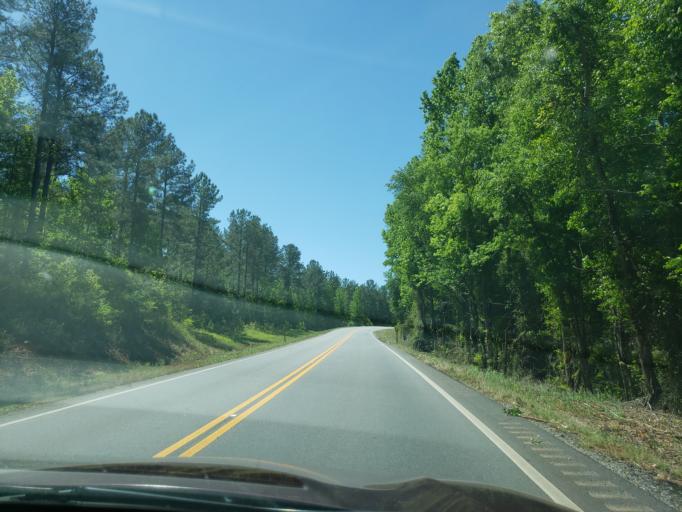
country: US
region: Alabama
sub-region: Tallapoosa County
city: Dadeville
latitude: 32.7029
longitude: -85.7858
